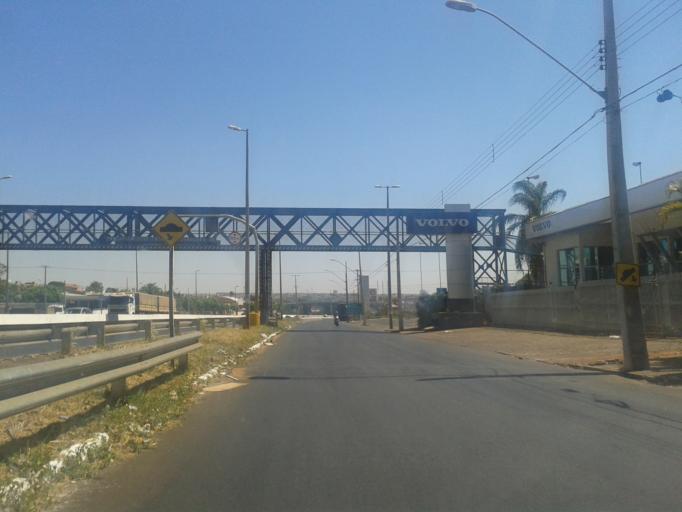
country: BR
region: Minas Gerais
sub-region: Uberlandia
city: Uberlandia
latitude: -18.9043
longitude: -48.2856
